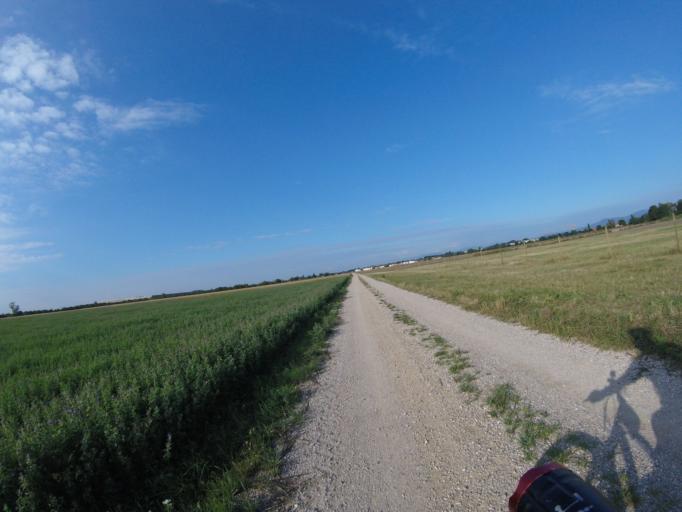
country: AT
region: Lower Austria
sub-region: Politischer Bezirk Baden
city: Trumau
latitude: 48.0029
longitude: 16.3616
